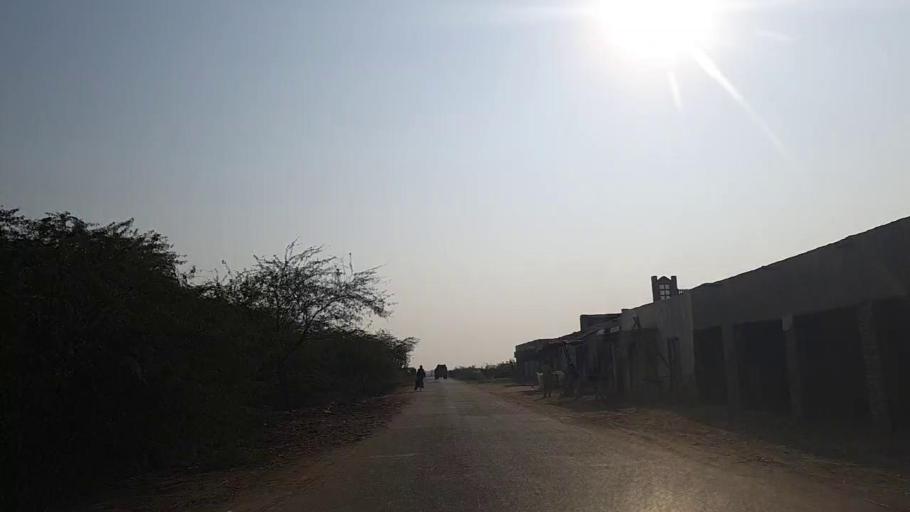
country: PK
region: Sindh
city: Jam Sahib
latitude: 26.2913
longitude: 68.6271
